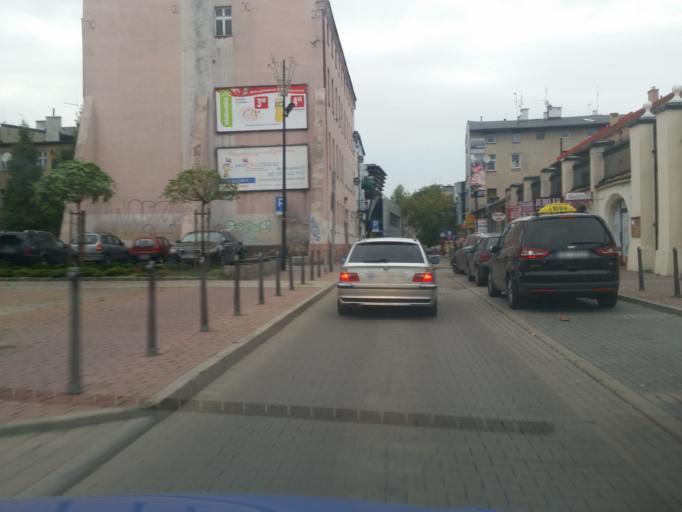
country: PL
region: Silesian Voivodeship
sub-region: Sosnowiec
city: Sosnowiec
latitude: 50.2748
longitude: 19.1309
